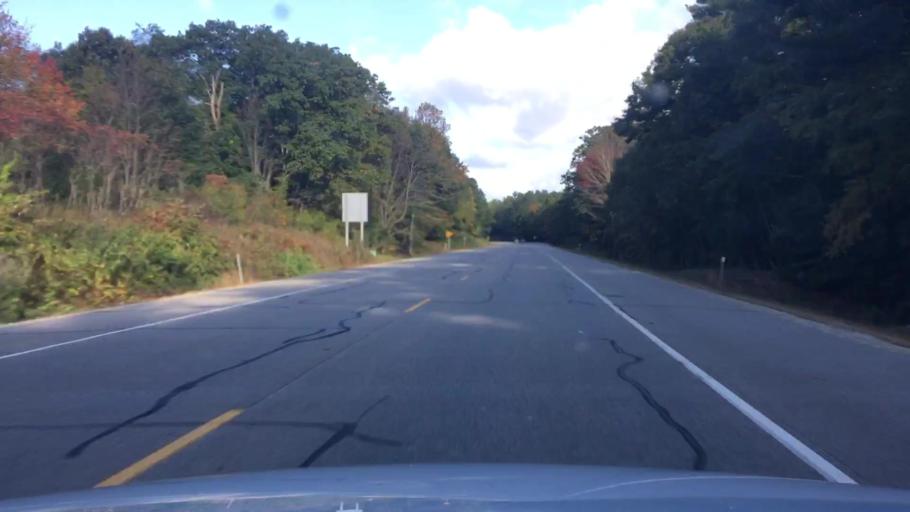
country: US
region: New Hampshire
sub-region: Strafford County
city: Durham
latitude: 43.1472
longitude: -70.9211
